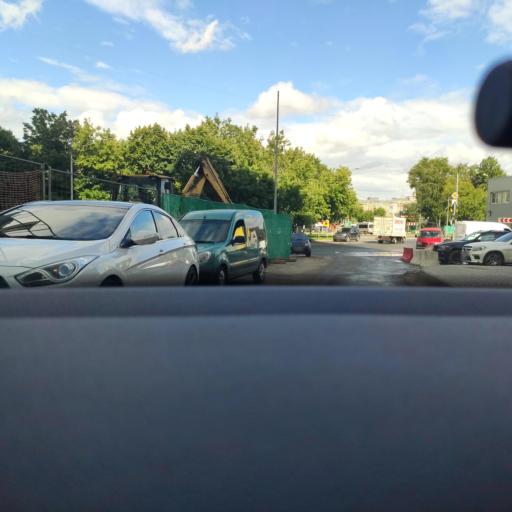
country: RU
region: Moscow
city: Sokol
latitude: 55.7865
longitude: 37.4983
